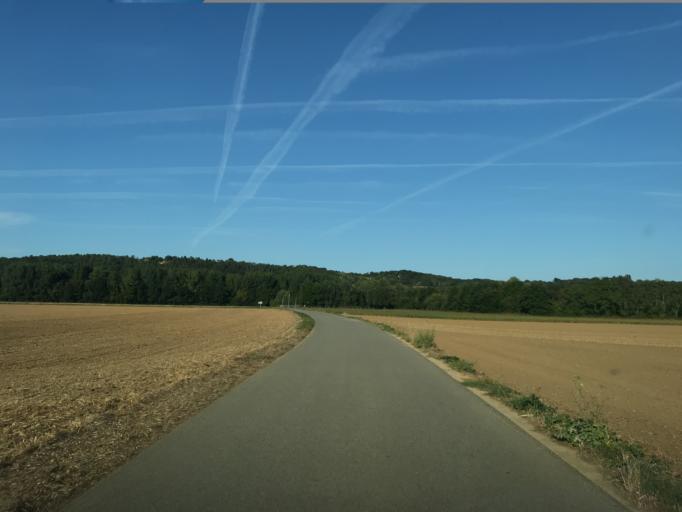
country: FR
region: Haute-Normandie
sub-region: Departement de l'Eure
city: Houlbec-Cocherel
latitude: 49.0556
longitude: 1.3127
